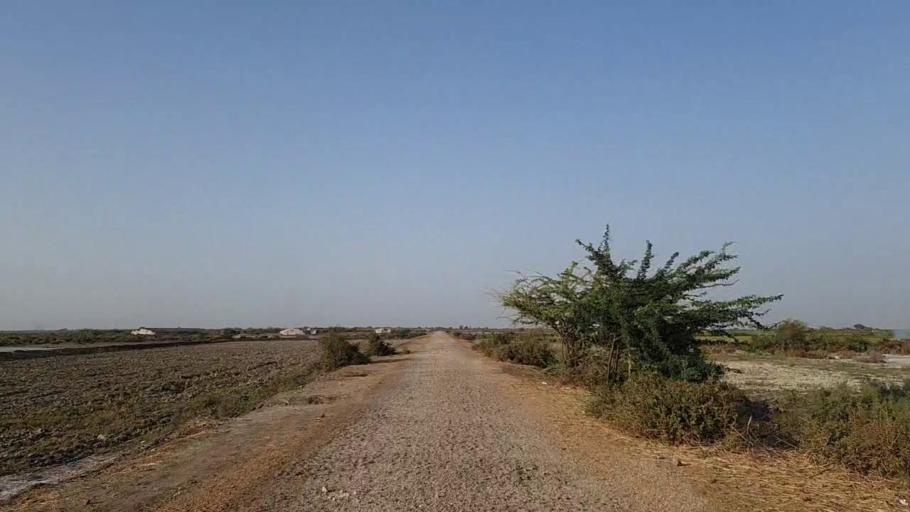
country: PK
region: Sindh
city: Jati
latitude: 24.3677
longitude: 68.1452
